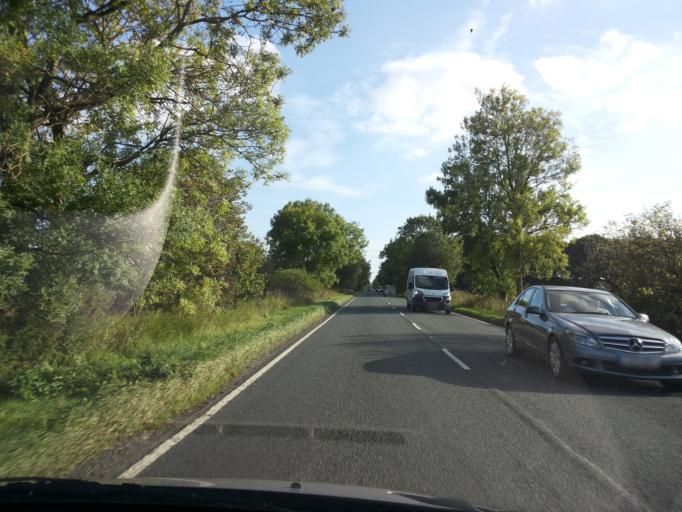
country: GB
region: England
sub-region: North Yorkshire
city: Camblesforth
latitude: 53.7441
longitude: -1.0478
